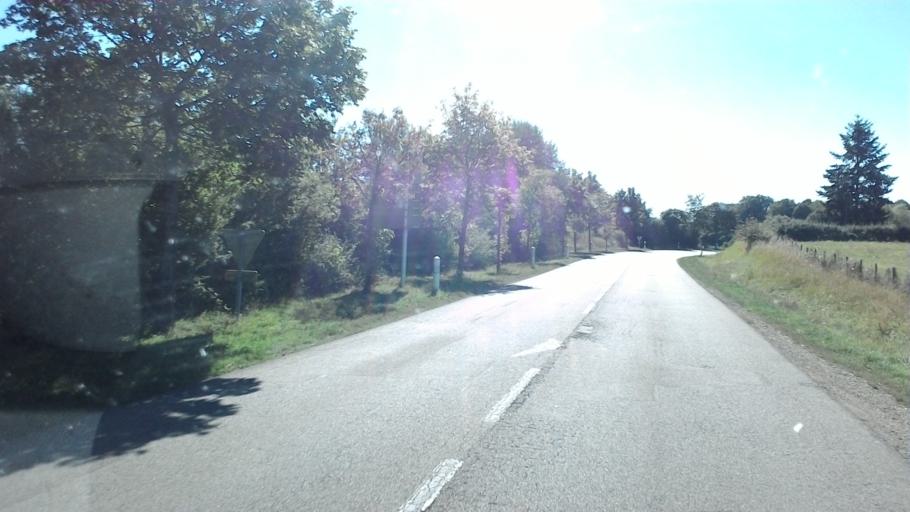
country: FR
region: Bourgogne
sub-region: Departement de la Cote-d'Or
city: Saulieu
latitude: 47.2761
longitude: 4.2386
